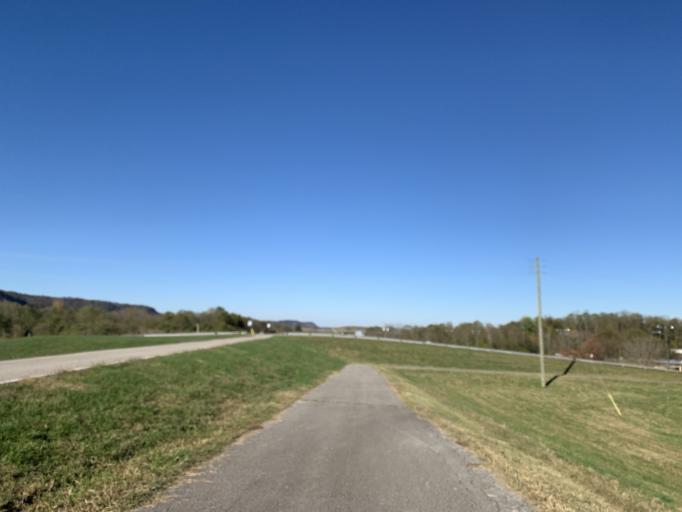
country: US
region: Kentucky
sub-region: Jefferson County
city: Pleasure Ridge Park
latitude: 38.1468
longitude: -85.9006
